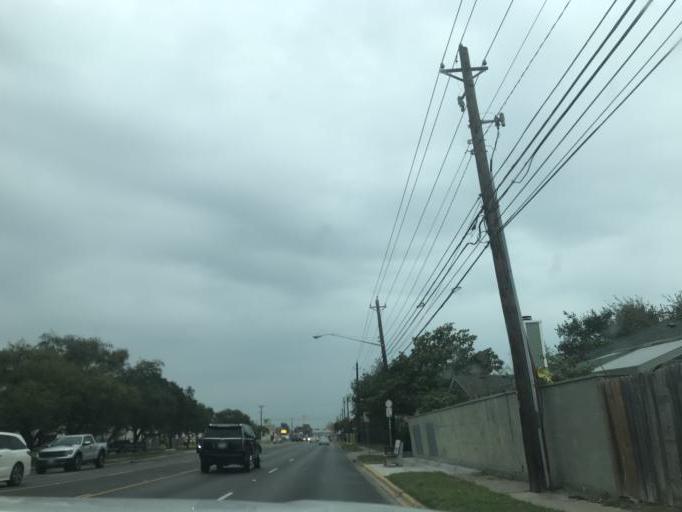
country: US
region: Texas
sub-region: Nueces County
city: Corpus Christi
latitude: 27.6965
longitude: -97.3631
